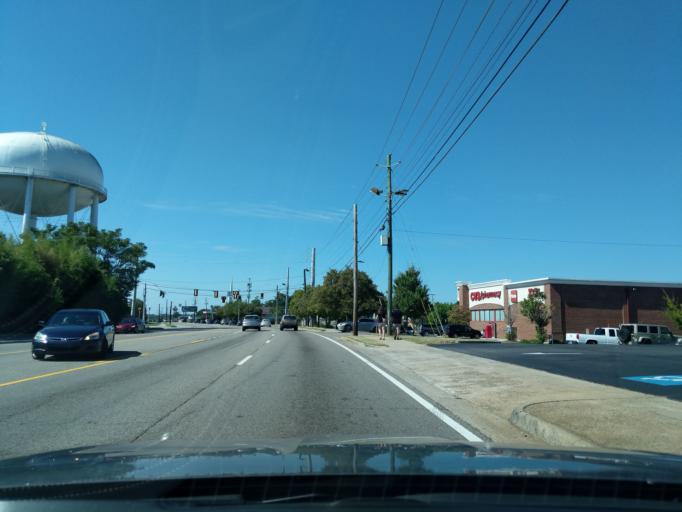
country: US
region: Georgia
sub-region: Columbia County
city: Martinez
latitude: 33.5080
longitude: -82.0216
